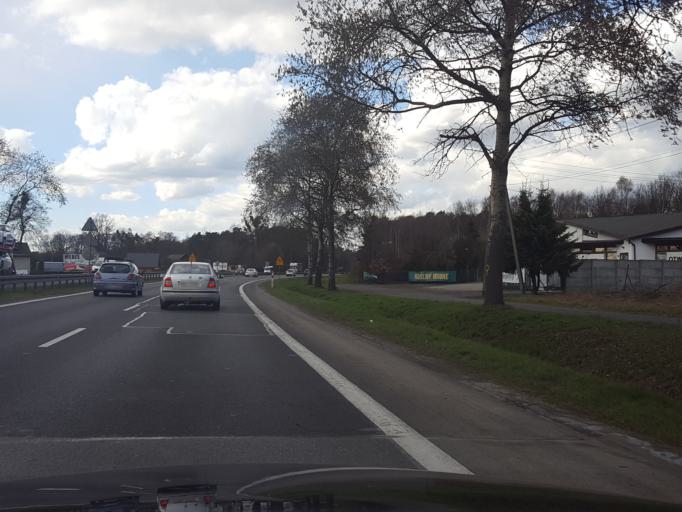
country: PL
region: Silesian Voivodeship
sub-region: Powiat pszczynski
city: Piasek
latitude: 50.0174
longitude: 18.9503
